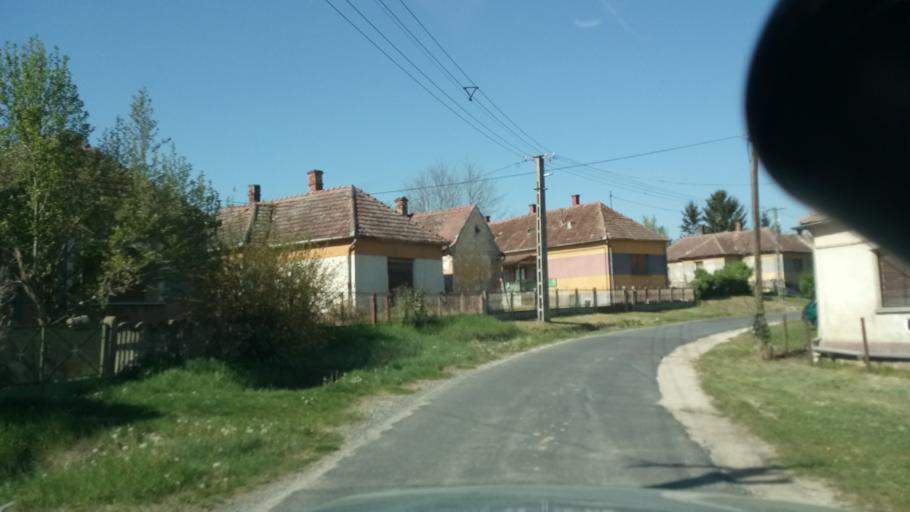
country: HU
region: Zala
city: Sarmellek
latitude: 46.7010
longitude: 17.1040
